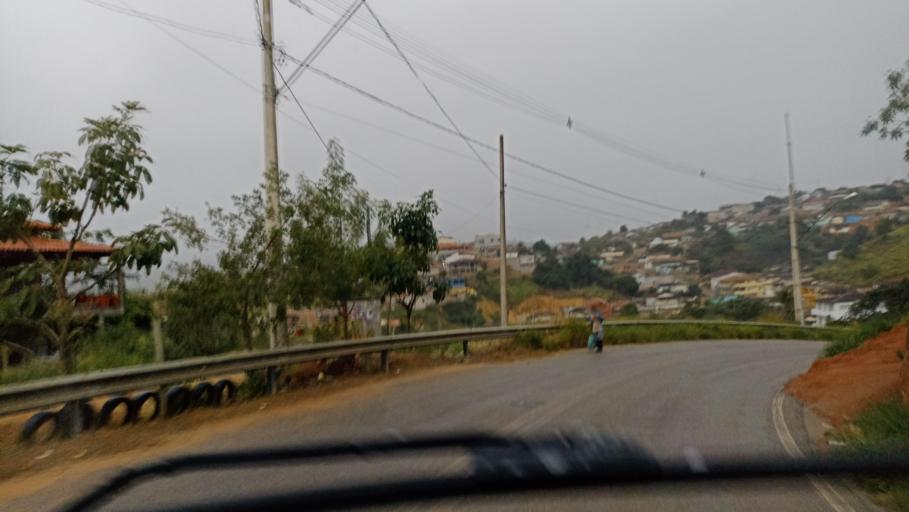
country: BR
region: Bahia
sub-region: Itanhem
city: Itanhem
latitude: -16.7347
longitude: -40.4267
